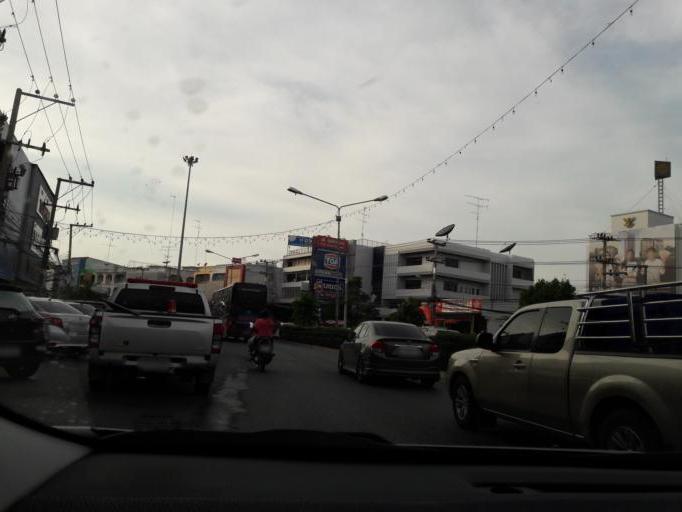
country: TH
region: Ang Thong
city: Ang Thong
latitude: 14.5934
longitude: 100.4516
